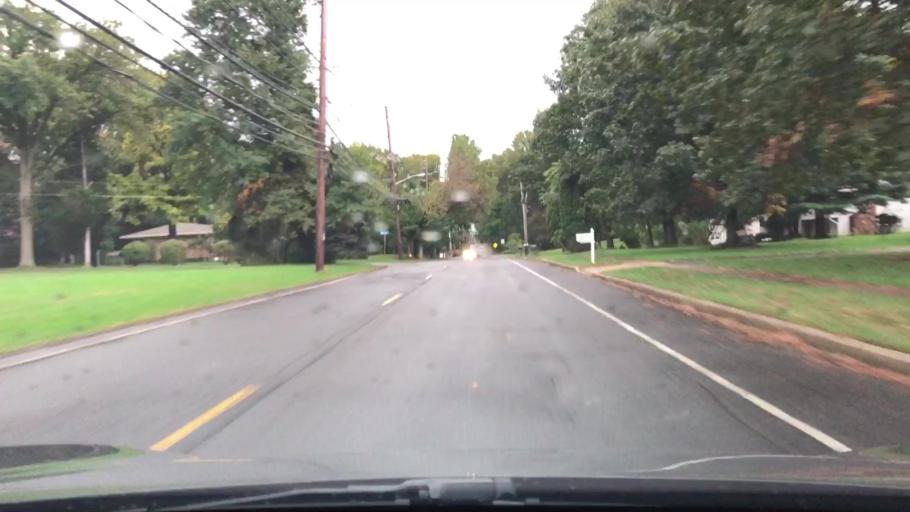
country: US
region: New Jersey
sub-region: Mercer County
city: Ewing
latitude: 40.2878
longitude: -74.7792
